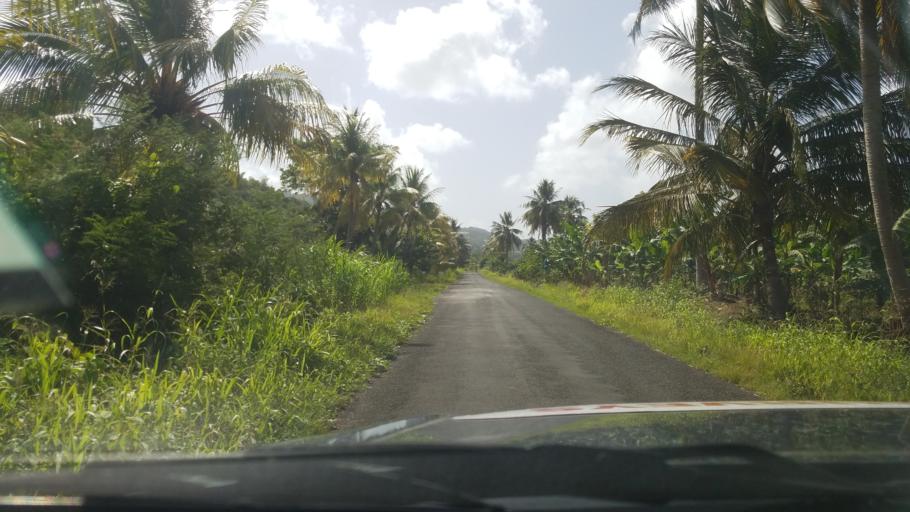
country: LC
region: Anse-la-Raye
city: Anse La Raye
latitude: 13.9564
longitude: -61.0145
